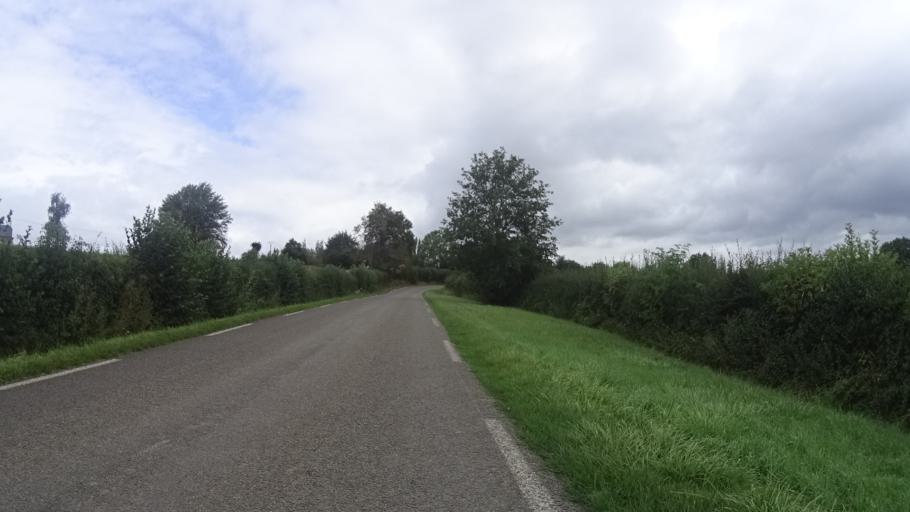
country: FR
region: Nord-Pas-de-Calais
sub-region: Departement du Nord
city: Berlaimont
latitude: 50.1890
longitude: 3.8070
